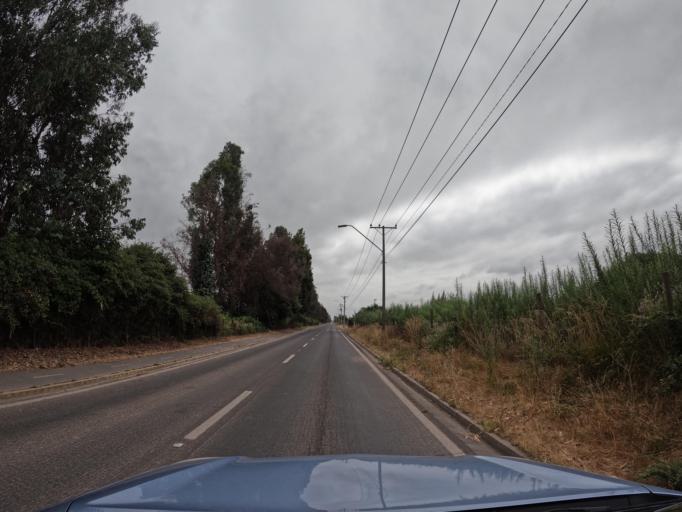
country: CL
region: O'Higgins
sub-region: Provincia de Colchagua
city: Chimbarongo
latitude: -34.7269
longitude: -71.0571
